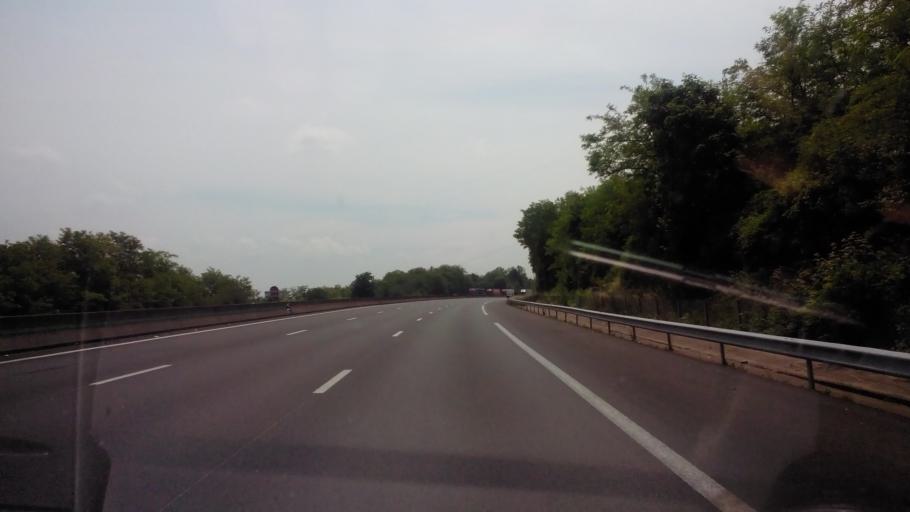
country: FR
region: Bourgogne
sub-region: Departement de Saone-et-Loire
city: Sance
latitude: 46.3345
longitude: 4.8201
